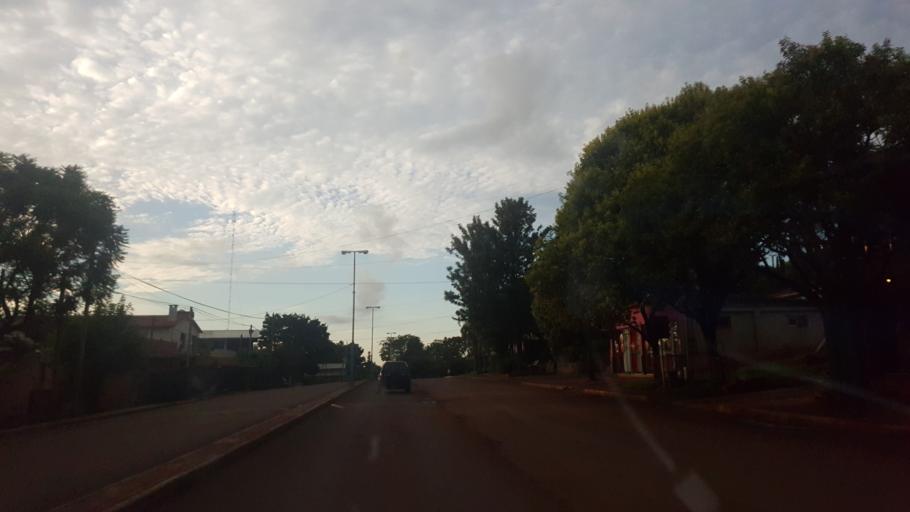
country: AR
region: Misiones
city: Dos de Mayo
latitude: -27.0227
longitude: -54.6865
